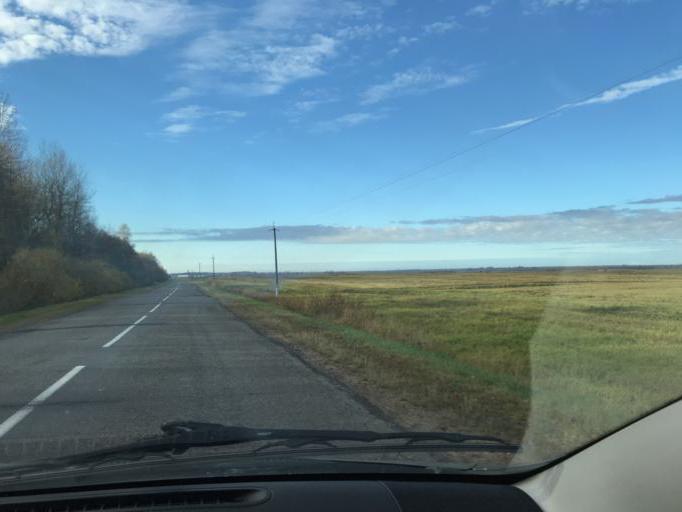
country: BY
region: Vitebsk
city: Haradok
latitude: 55.3905
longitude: 29.6720
